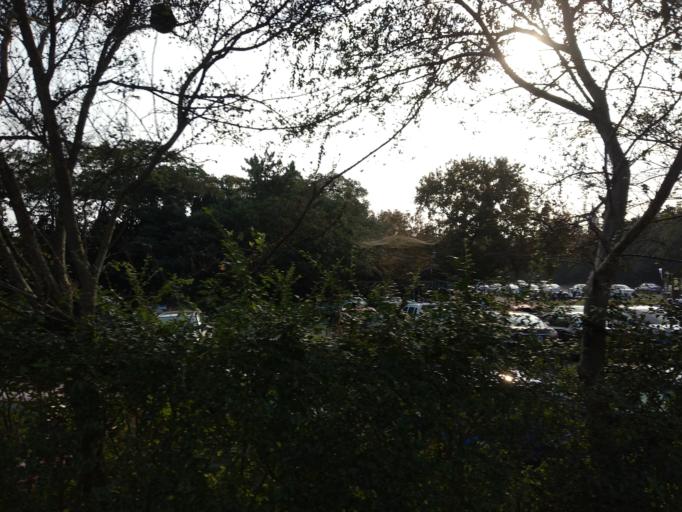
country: TW
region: Taiwan
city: Daxi
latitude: 24.8230
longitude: 121.1835
